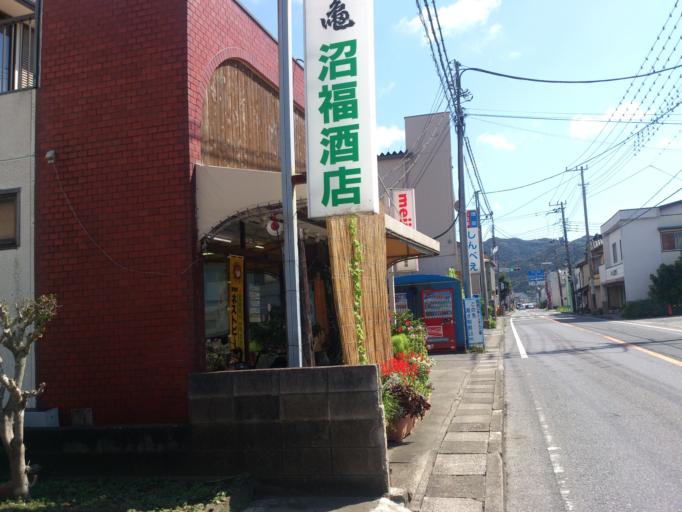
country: JP
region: Chiba
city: Tateyama
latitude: 35.0932
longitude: 139.8484
